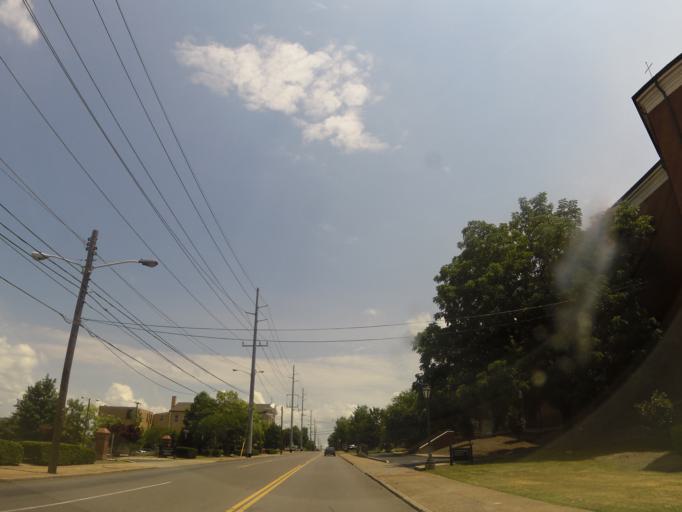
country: US
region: Tennessee
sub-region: Davidson County
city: Nashville
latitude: 36.1719
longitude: -86.7645
